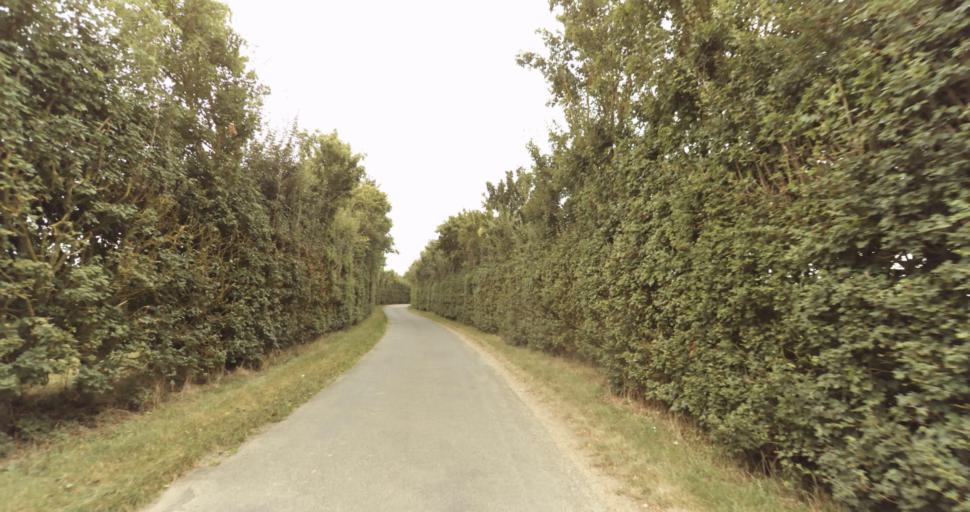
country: FR
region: Haute-Normandie
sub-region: Departement de l'Eure
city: Gravigny
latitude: 49.0365
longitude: 1.2135
